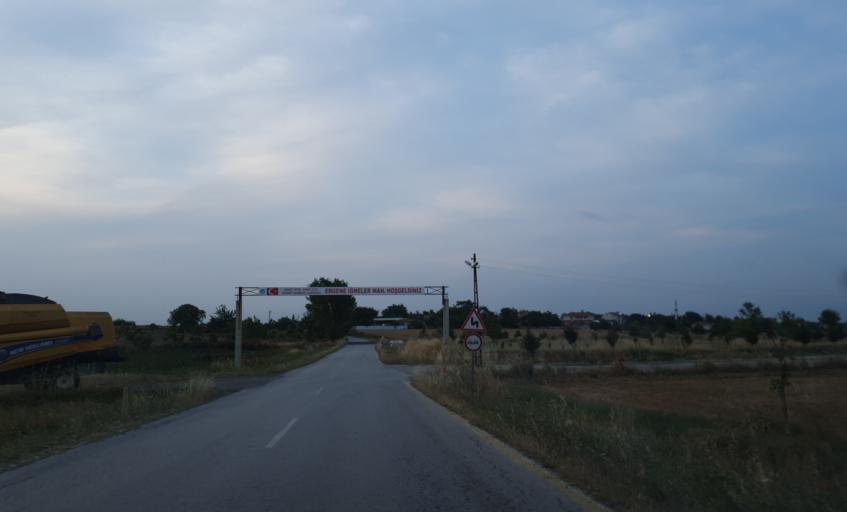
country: TR
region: Kirklareli
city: Buyukkaristiran
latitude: 41.3406
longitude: 27.6049
